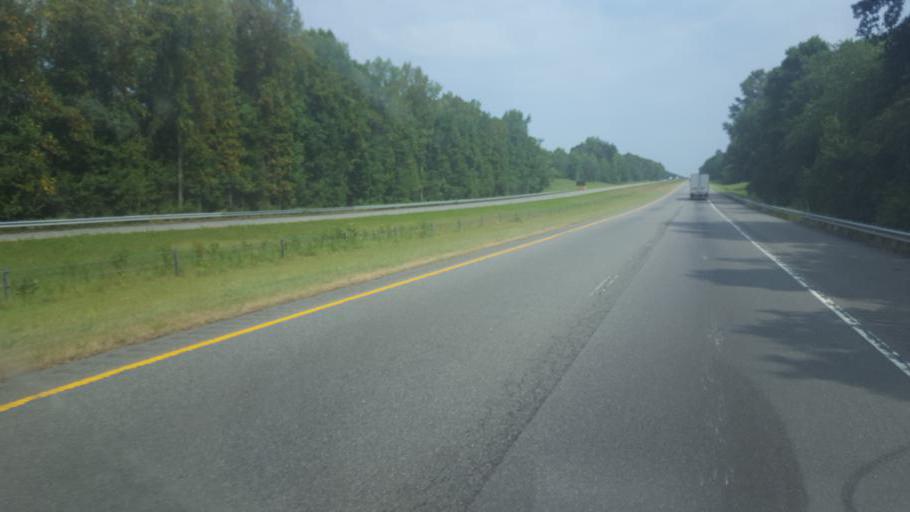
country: US
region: North Carolina
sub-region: Iredell County
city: Statesville
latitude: 35.9434
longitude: -80.8522
